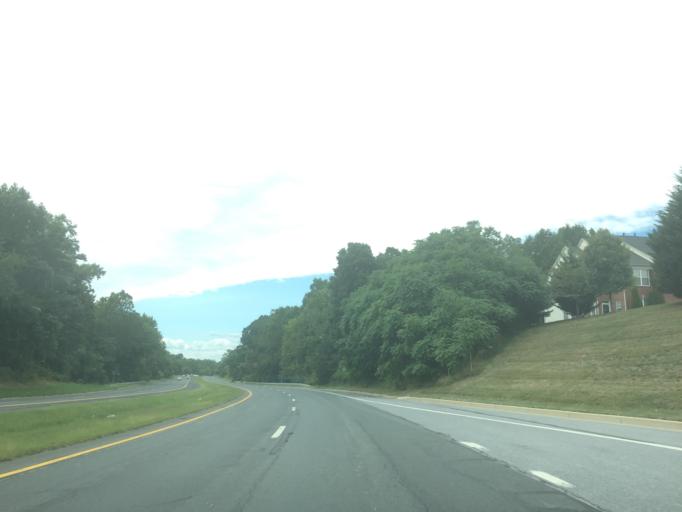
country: US
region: Maryland
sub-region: Montgomery County
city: Gaithersburg
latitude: 39.1570
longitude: -77.1840
